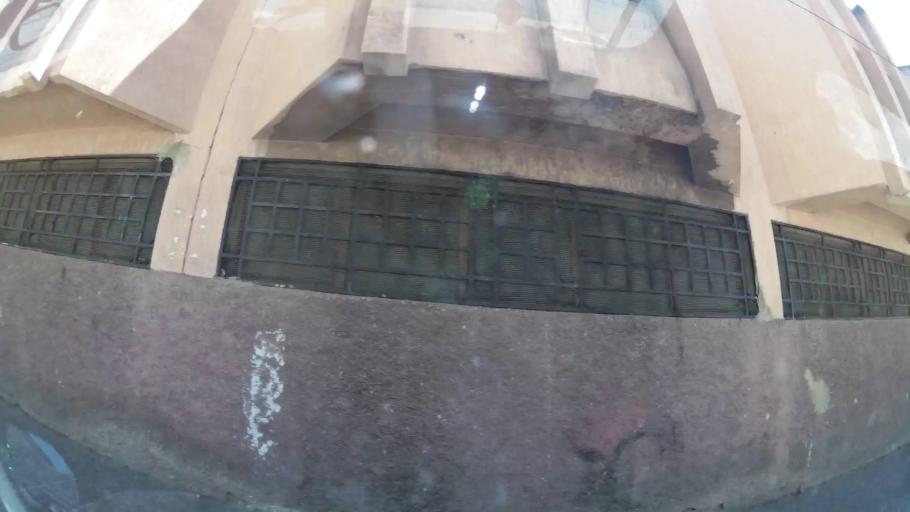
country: MA
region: Meknes-Tafilalet
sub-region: Meknes
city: Meknes
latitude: 33.9048
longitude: -5.5768
